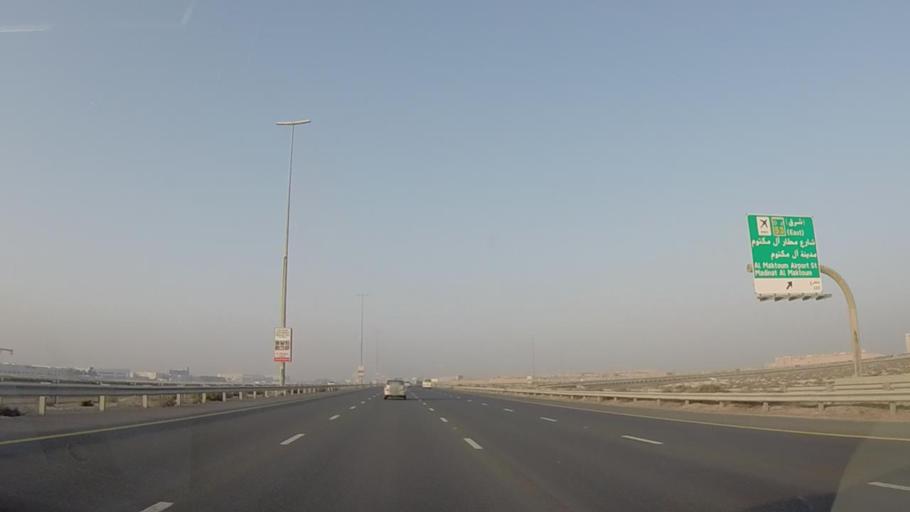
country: AE
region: Dubai
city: Dubai
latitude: 24.9435
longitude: 55.0519
